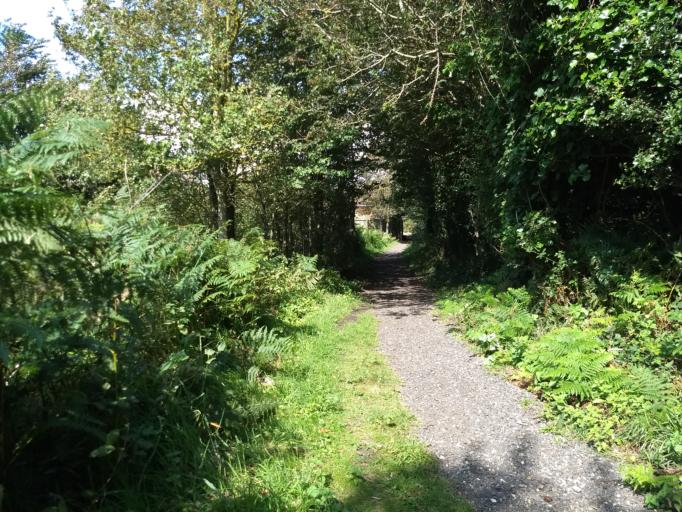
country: GB
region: England
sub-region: Isle of Wight
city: Totland
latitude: 50.6850
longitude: -1.5407
